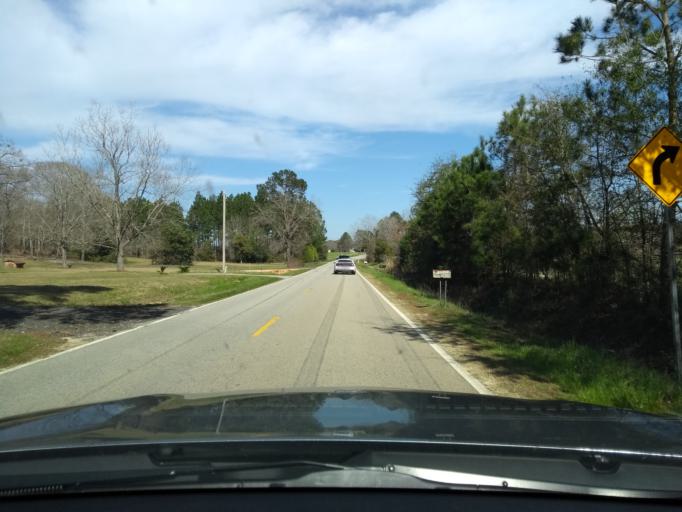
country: US
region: Georgia
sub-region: Bulloch County
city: Brooklet
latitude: 32.4679
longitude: -81.6444
